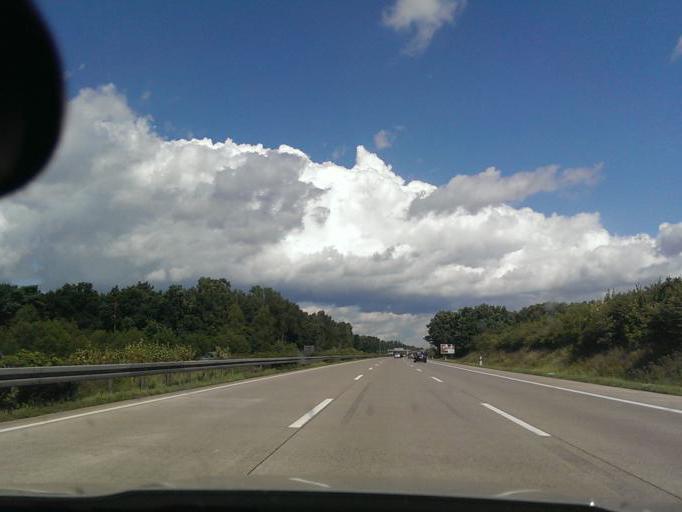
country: DE
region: Lower Saxony
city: Isernhagen Farster Bauerschaft
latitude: 52.5046
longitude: 9.8248
